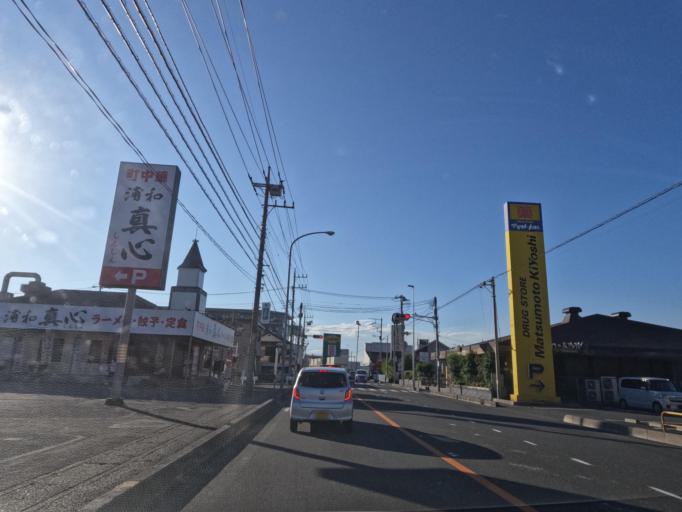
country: JP
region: Saitama
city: Shimotoda
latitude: 35.8590
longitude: 139.6767
